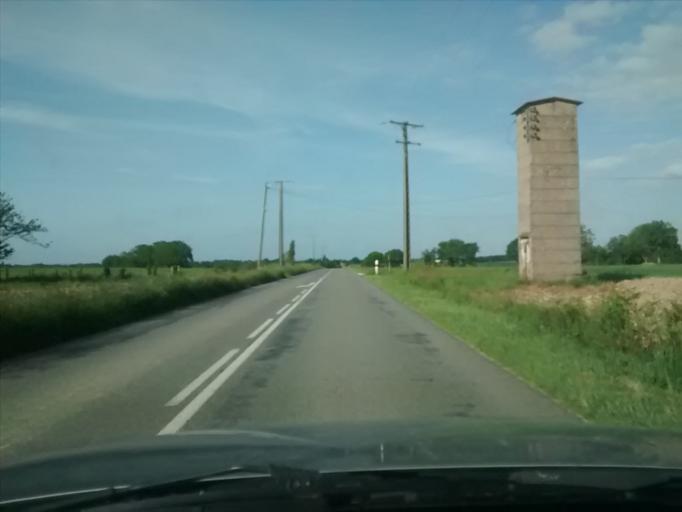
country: FR
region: Pays de la Loire
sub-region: Departement de la Mayenne
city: Meslay-du-Maine
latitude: 47.9436
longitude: -0.6370
